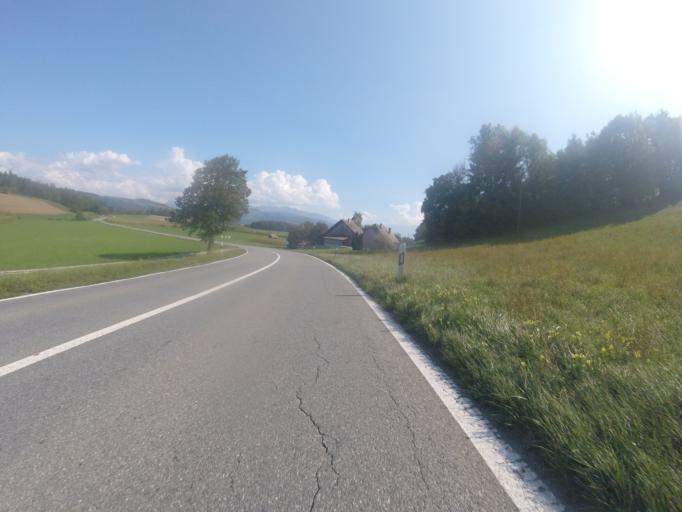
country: CH
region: Bern
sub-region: Thun District
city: Uttigen
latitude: 46.7890
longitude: 7.5602
